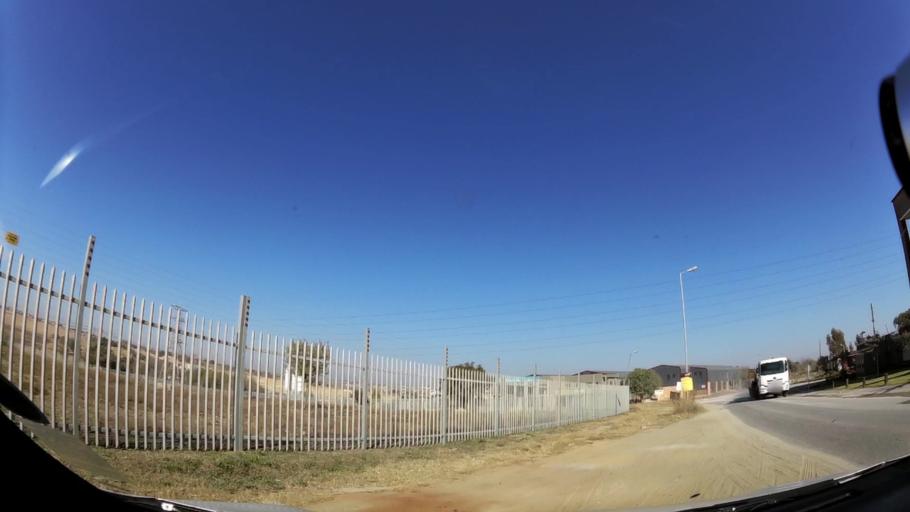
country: ZA
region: Gauteng
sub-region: City of Johannesburg Metropolitan Municipality
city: Midrand
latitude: -25.9194
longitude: 28.1256
